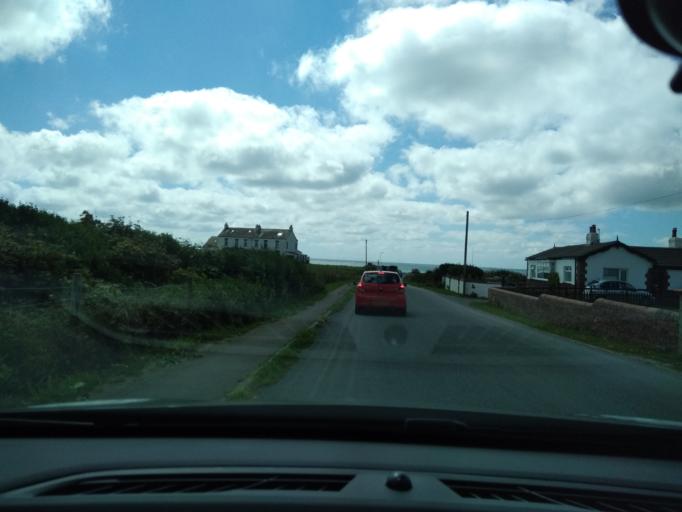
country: GB
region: England
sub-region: Cumbria
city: Millom
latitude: 54.2186
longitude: -3.3476
